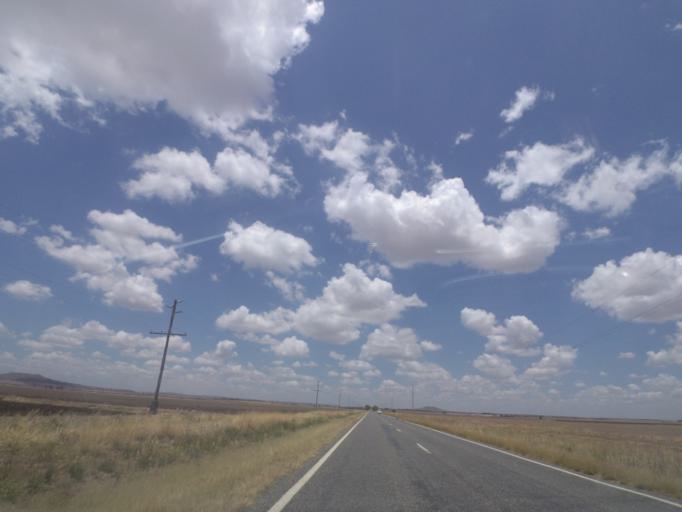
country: AU
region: Queensland
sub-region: Toowoomba
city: Top Camp
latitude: -27.9073
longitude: 151.9784
